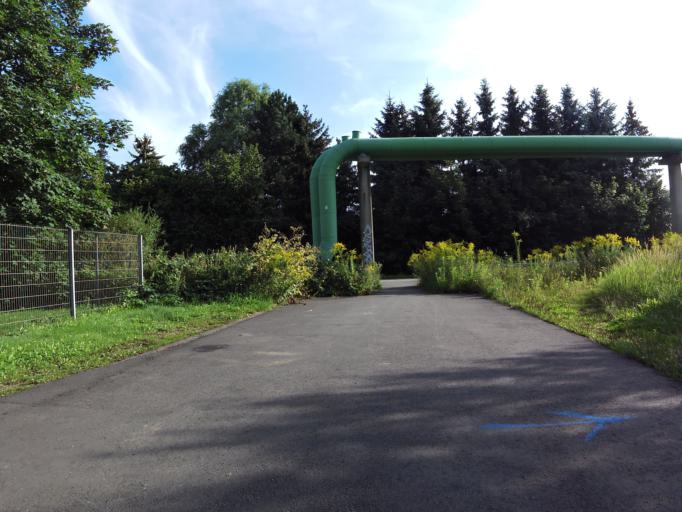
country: DE
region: Saxony
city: Taucha
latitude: 51.3498
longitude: 12.4642
